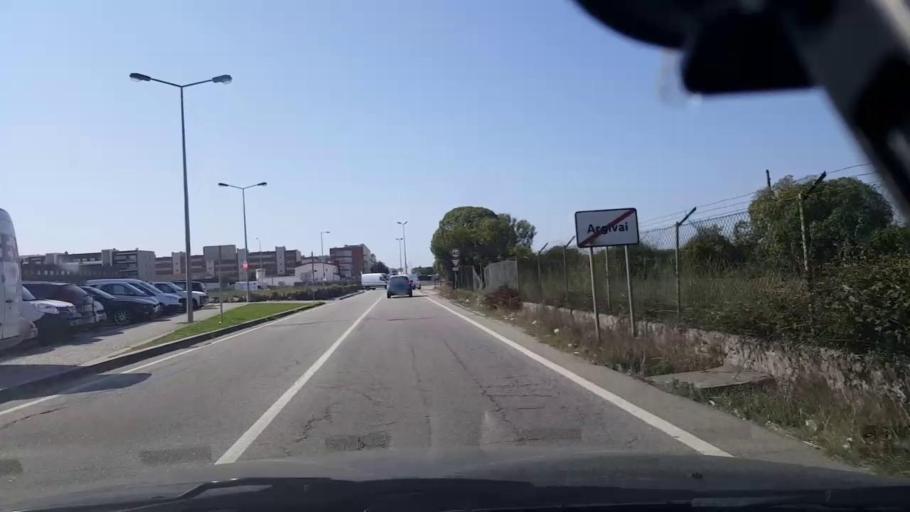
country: PT
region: Porto
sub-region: Vila do Conde
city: Vila do Conde
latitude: 41.3723
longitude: -8.7445
